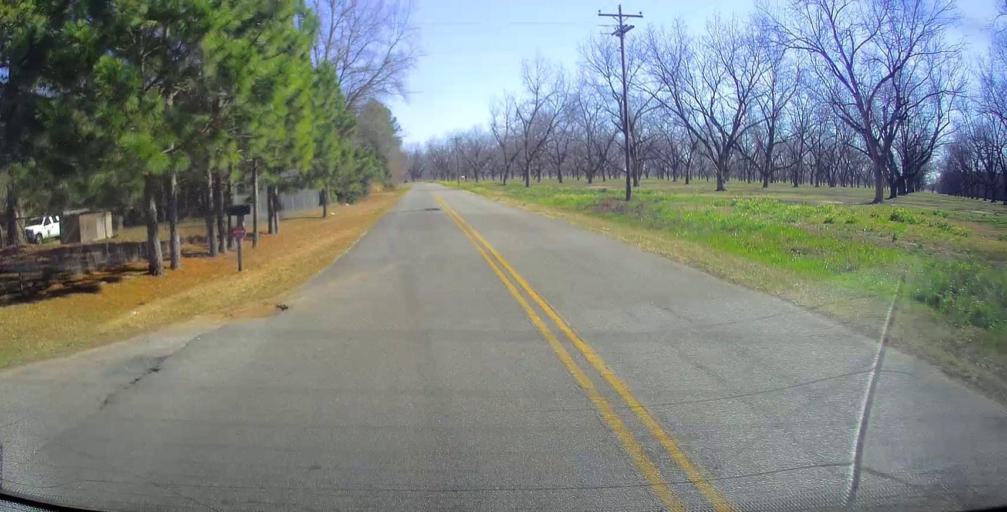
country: US
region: Georgia
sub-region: Peach County
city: Fort Valley
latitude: 32.6313
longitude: -83.8504
